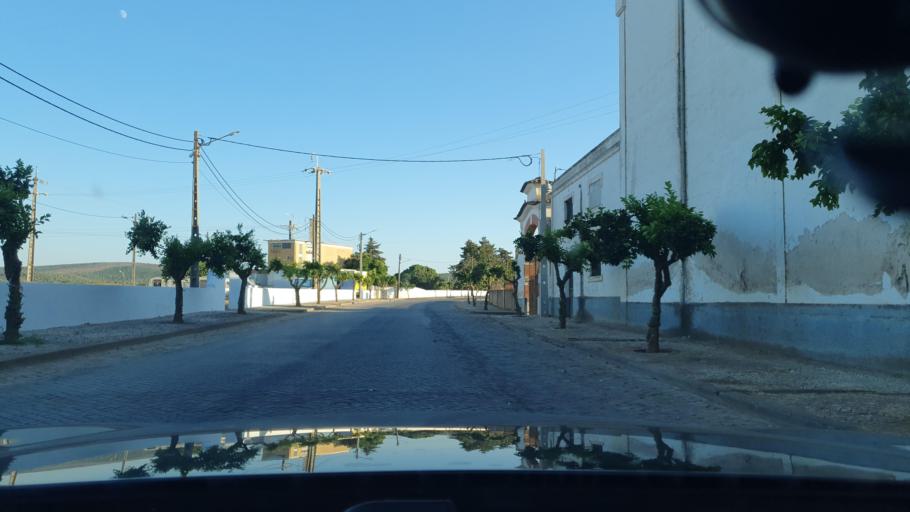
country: PT
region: Portalegre
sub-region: Fronteira
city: Fronteira
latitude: 38.9495
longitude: -7.6758
